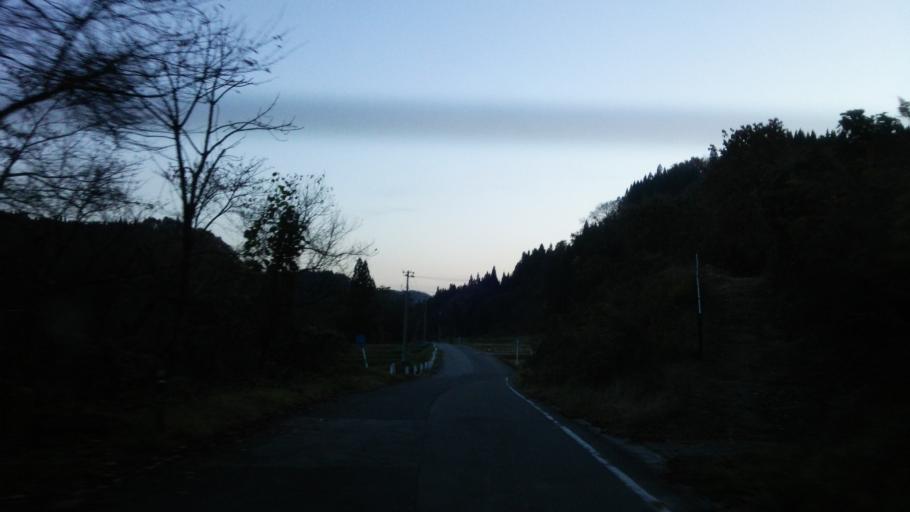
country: JP
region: Fukushima
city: Kitakata
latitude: 37.5192
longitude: 139.7053
